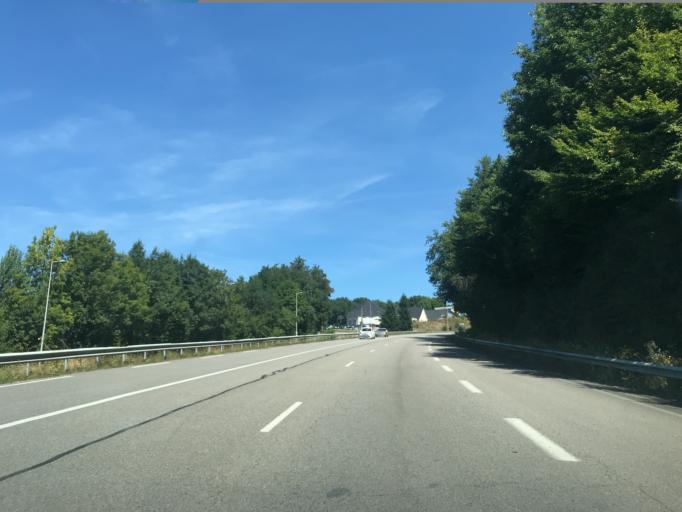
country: FR
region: Limousin
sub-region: Departement de la Correze
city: Tulle
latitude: 45.2764
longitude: 1.7891
